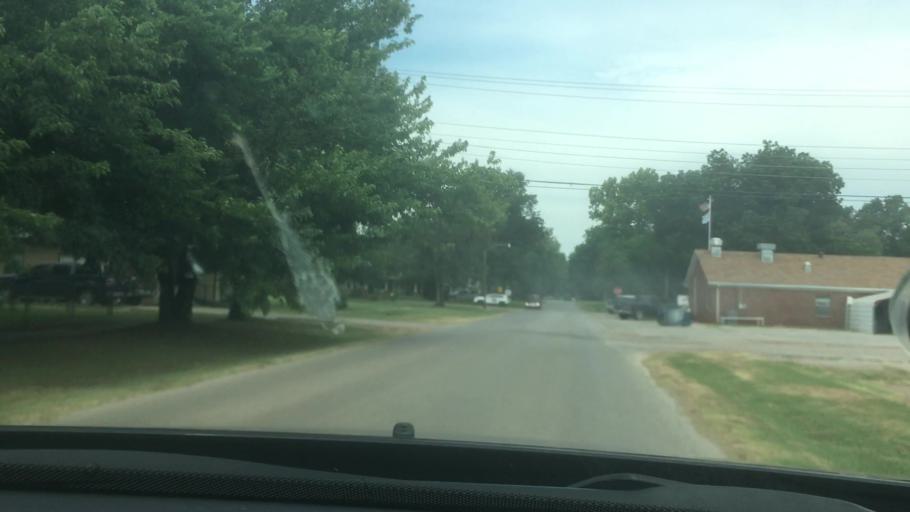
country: US
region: Oklahoma
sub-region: Garvin County
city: Lindsay
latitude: 34.8359
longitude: -97.6059
